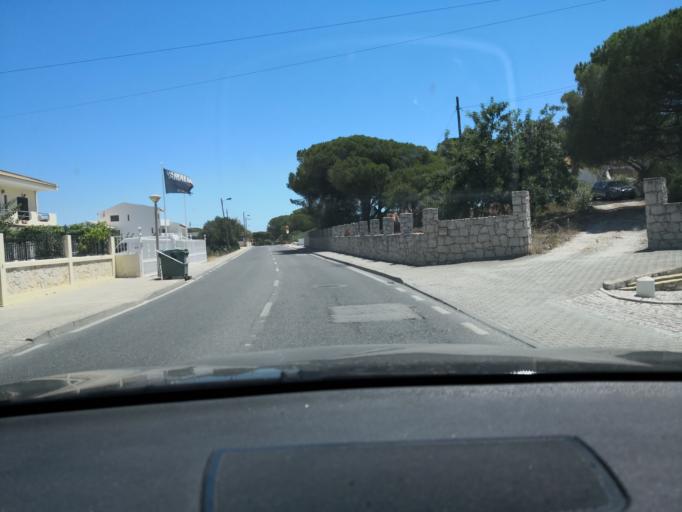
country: PT
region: Faro
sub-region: Albufeira
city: Ferreiras
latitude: 37.1083
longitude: -8.2080
